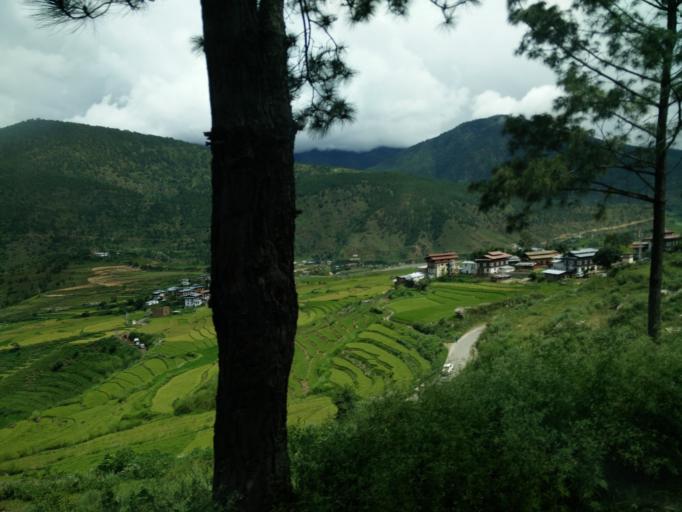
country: BT
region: Punakha
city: Pajo
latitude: 27.5222
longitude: 89.8670
